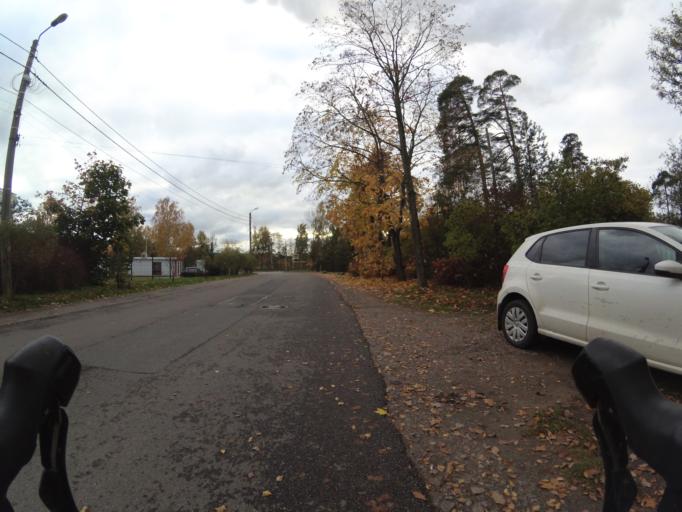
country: RU
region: St.-Petersburg
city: Lakhtinskiy
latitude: 59.9964
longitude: 30.1451
